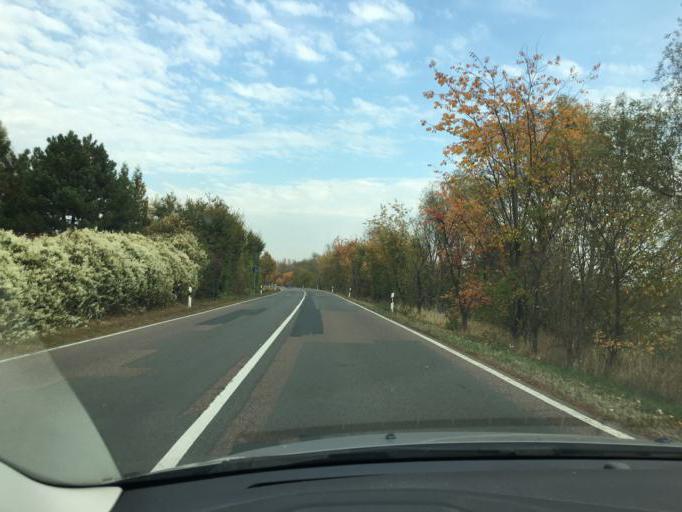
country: DE
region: Saxony
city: Zwochau
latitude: 51.4903
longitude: 12.2749
